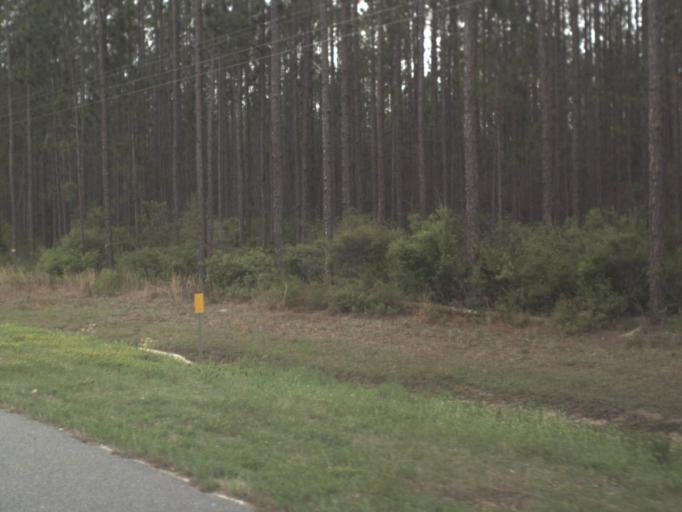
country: US
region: Florida
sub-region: Gulf County
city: Wewahitchka
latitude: 30.3148
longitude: -85.2317
